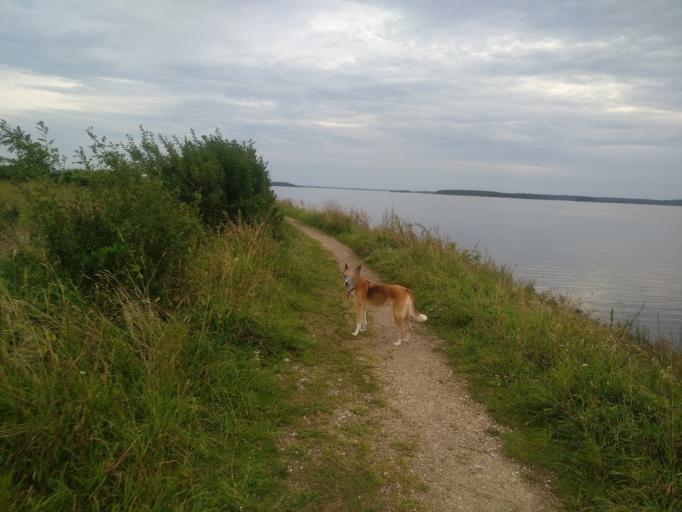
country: RU
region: Tverskaya
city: Vyshniy Volochek
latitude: 57.6062
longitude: 34.4967
